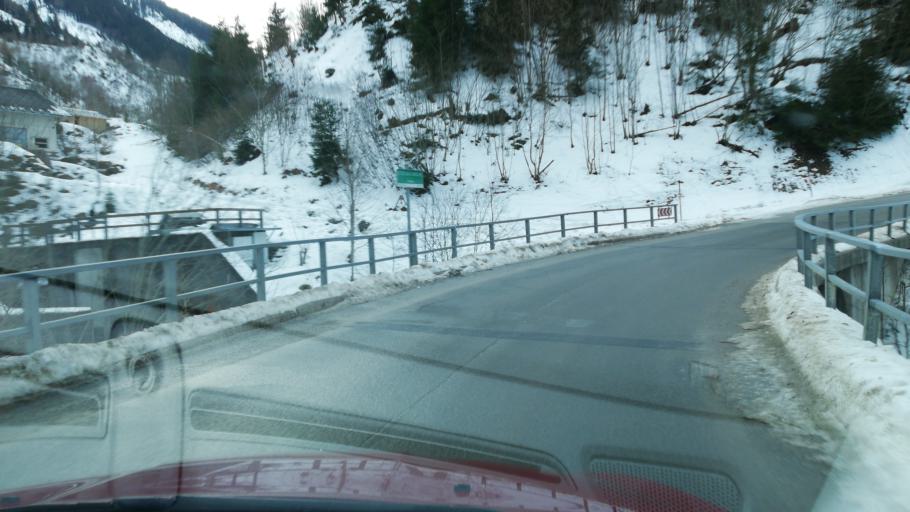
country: AT
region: Styria
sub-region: Politischer Bezirk Liezen
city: Donnersbach
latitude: 47.4347
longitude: 14.1576
